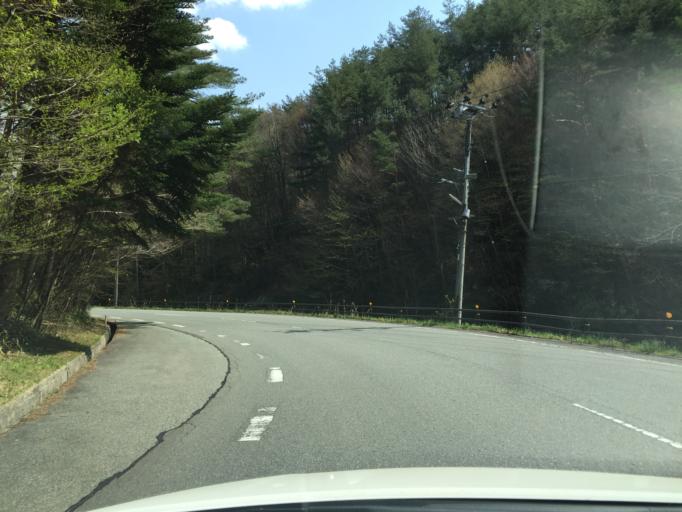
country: JP
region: Fukushima
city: Namie
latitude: 37.3715
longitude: 140.8018
